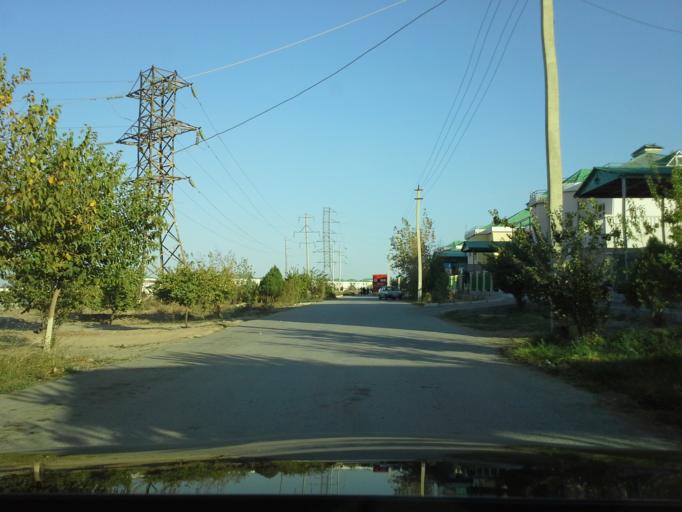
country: TM
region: Ahal
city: Abadan
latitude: 38.0507
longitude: 58.1704
